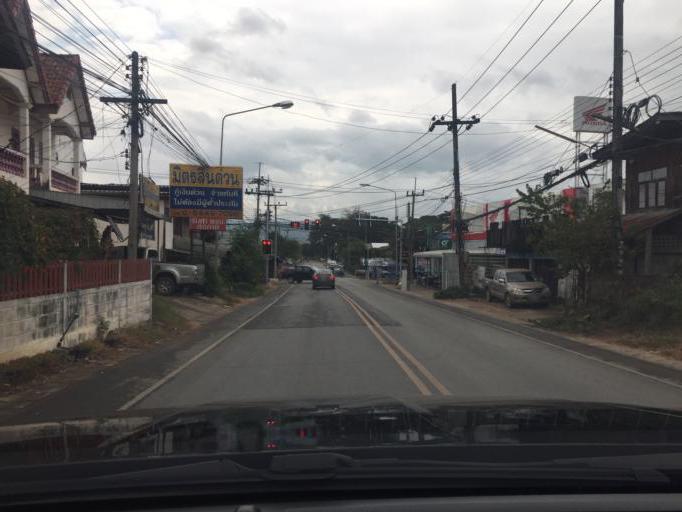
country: TH
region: Phayao
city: Pong
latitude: 19.1708
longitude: 100.2828
